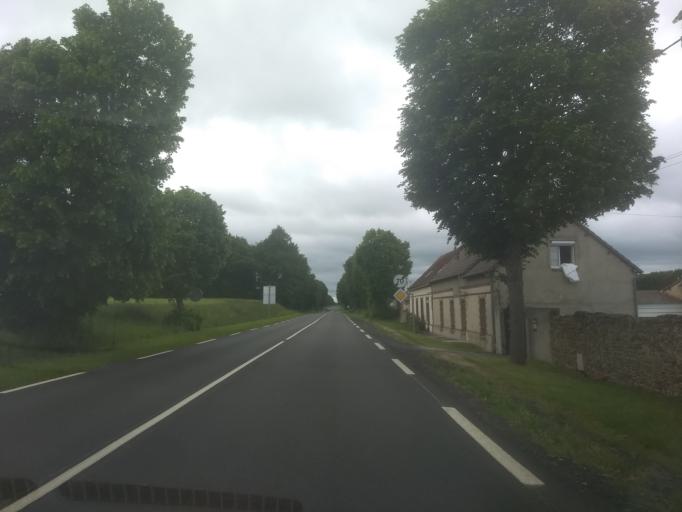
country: FR
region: Centre
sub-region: Departement d'Eure-et-Loir
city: Treon
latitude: 48.6383
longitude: 1.2757
